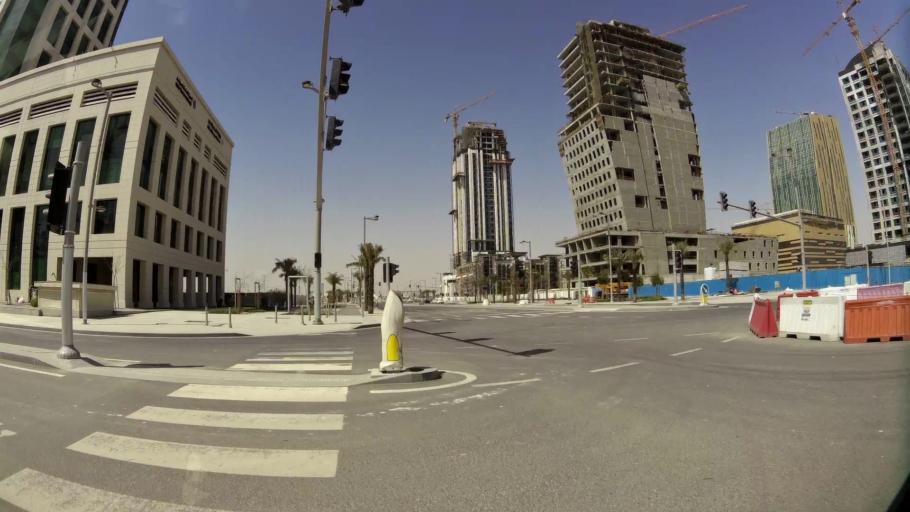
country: QA
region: Baladiyat ad Dawhah
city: Doha
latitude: 25.3946
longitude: 51.5219
